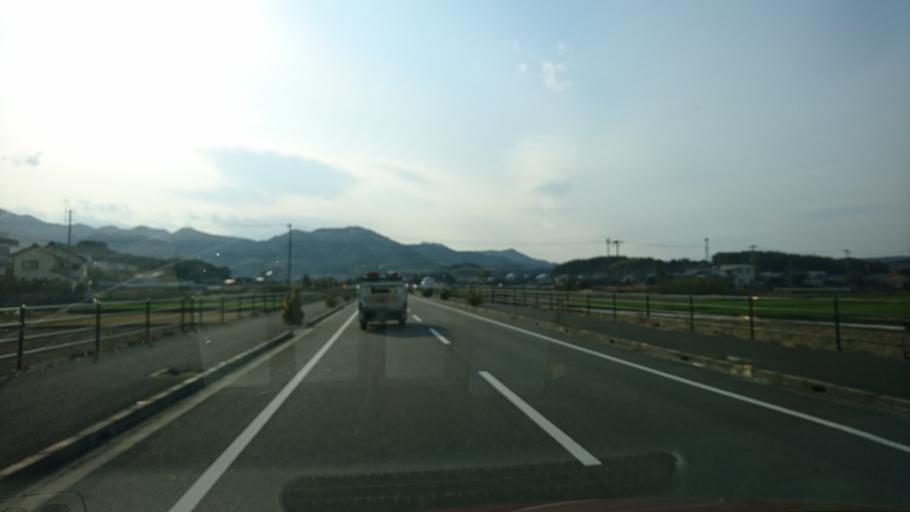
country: JP
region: Ehime
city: Saijo
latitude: 34.0249
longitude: 133.0007
